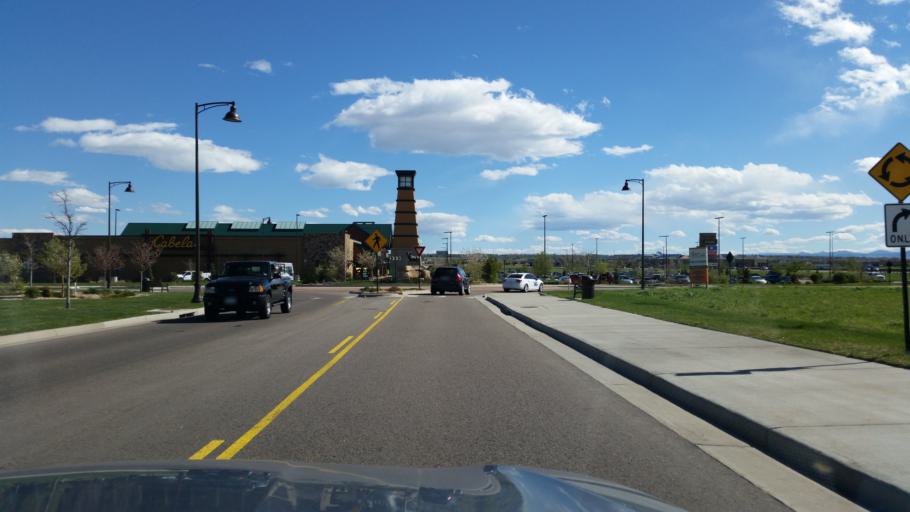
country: US
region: Colorado
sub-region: Adams County
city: Northglenn
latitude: 39.9535
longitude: -104.9863
